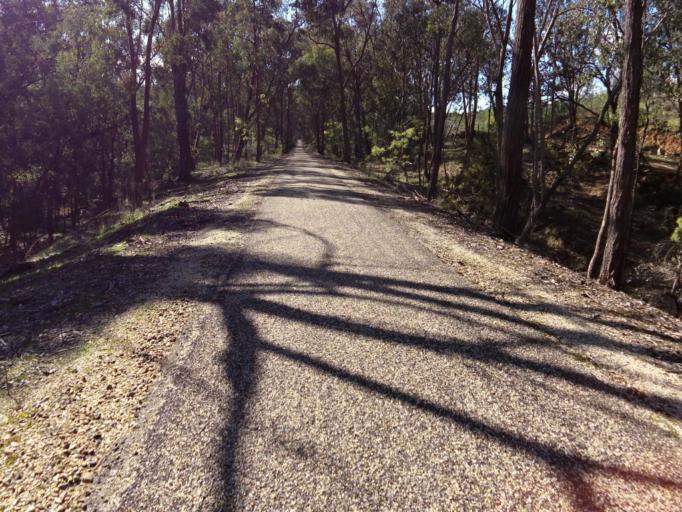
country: AU
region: Victoria
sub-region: Wangaratta
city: Wangaratta
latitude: -36.4046
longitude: 146.6284
